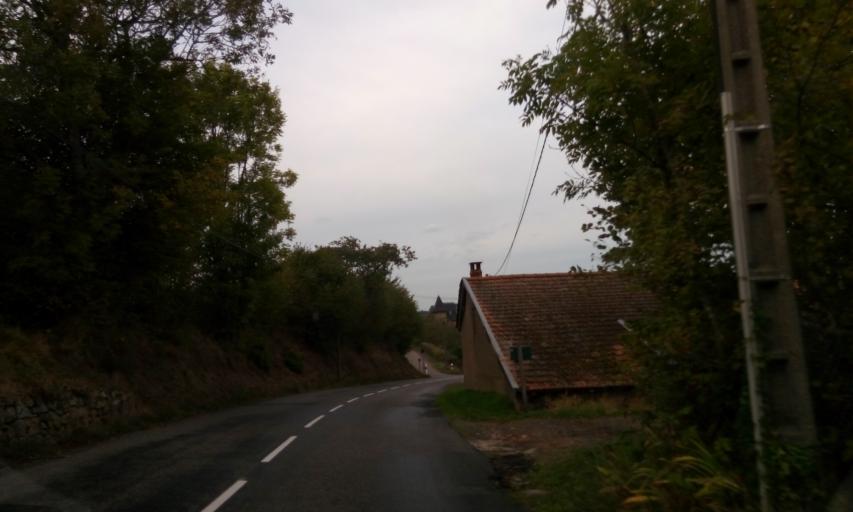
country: FR
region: Rhone-Alpes
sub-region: Departement du Rhone
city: Cublize
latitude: 45.9992
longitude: 4.4317
